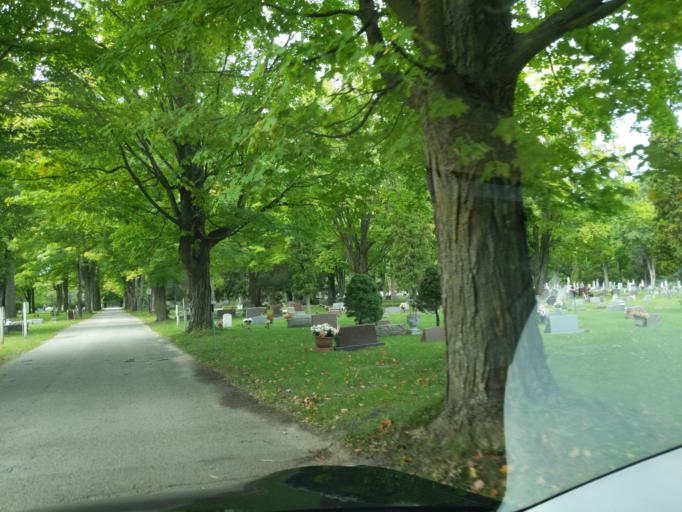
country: US
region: Michigan
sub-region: Grand Traverse County
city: Traverse City
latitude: 44.7544
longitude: -85.5848
